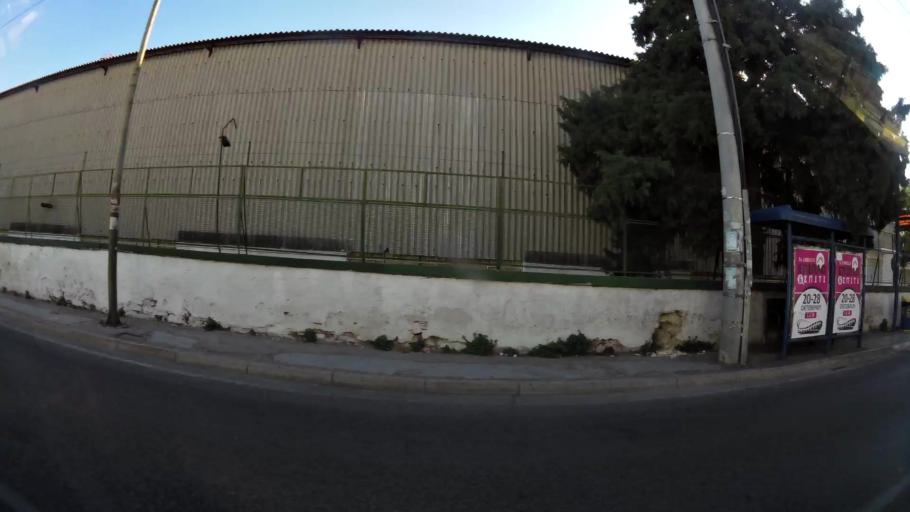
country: GR
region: Attica
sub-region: Nomos Piraios
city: Perama
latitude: 37.9633
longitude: 23.5659
